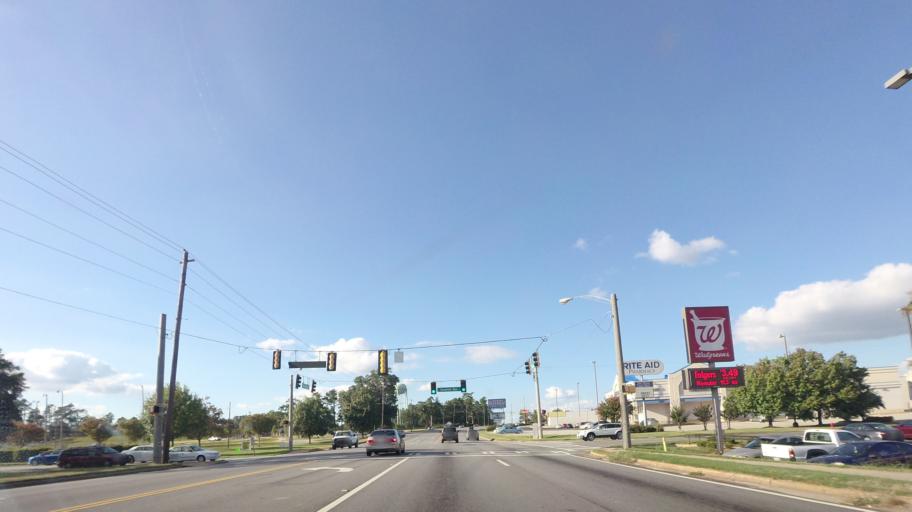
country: US
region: Georgia
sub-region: Upson County
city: Thomaston
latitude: 32.9024
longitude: -84.3293
